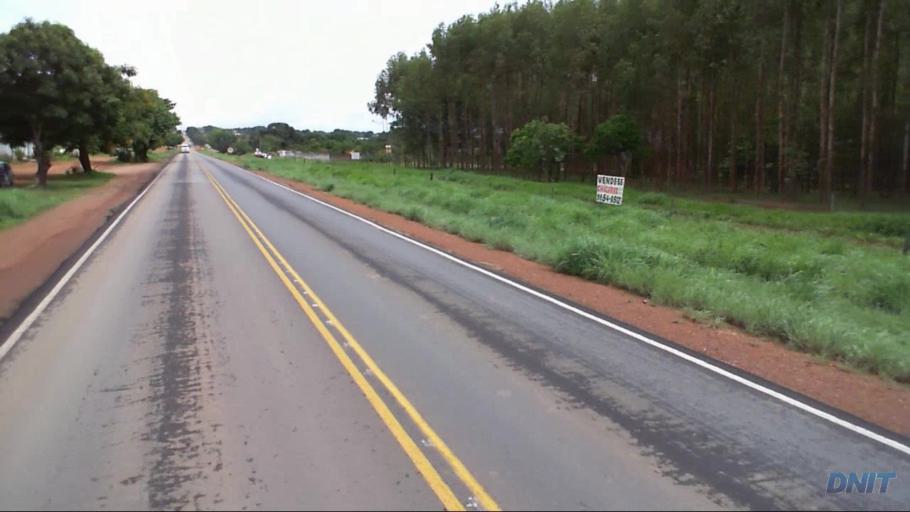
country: BR
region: Goias
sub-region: Padre Bernardo
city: Padre Bernardo
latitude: -15.2675
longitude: -48.2636
